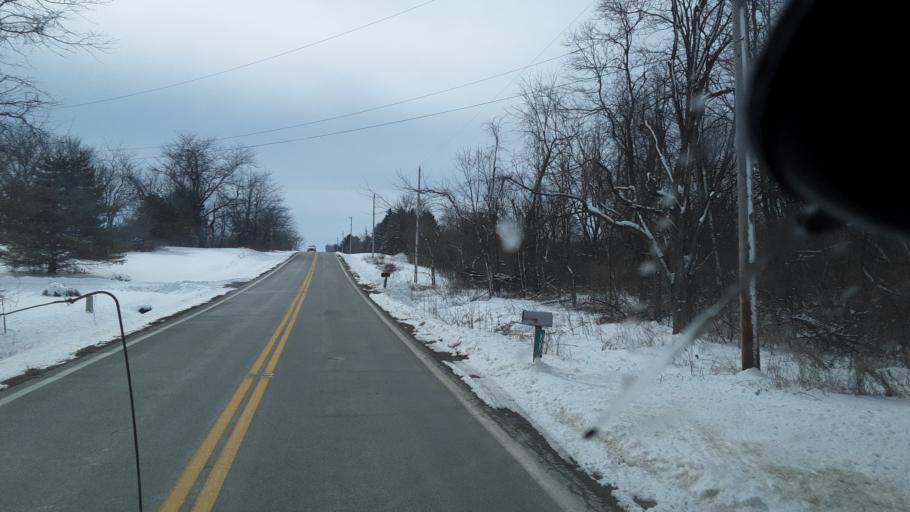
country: US
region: Ohio
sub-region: Madison County
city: Choctaw Lake
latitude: 39.9777
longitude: -83.5001
